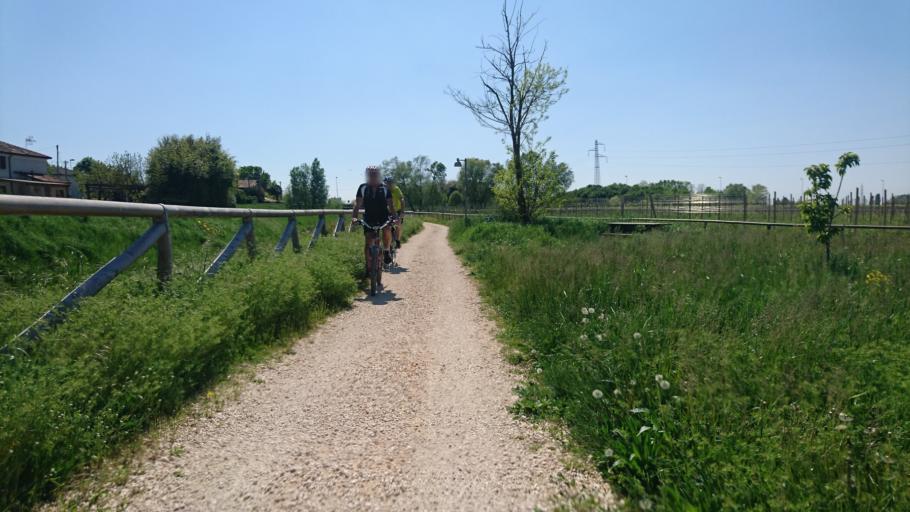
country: IT
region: Veneto
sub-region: Provincia di Treviso
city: Dosson
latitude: 45.6305
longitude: 12.2704
